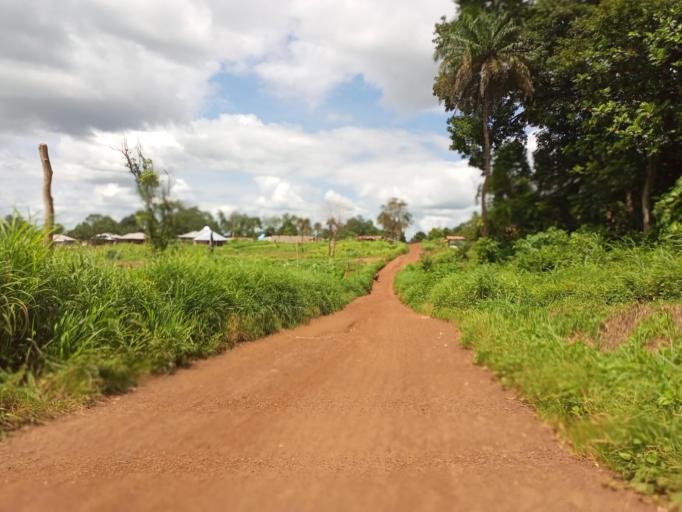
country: SL
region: Northern Province
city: Kamakwie
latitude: 9.5001
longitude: -12.2385
